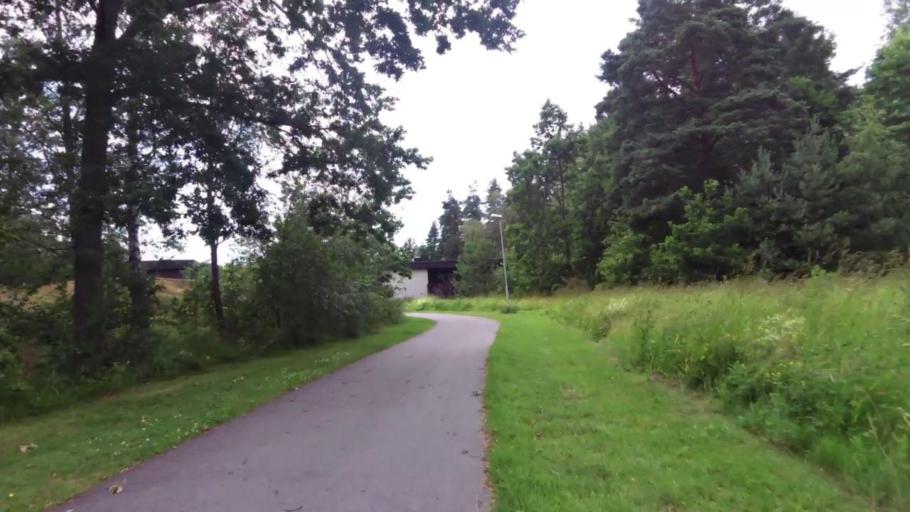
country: SE
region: OEstergoetland
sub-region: Linkopings Kommun
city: Malmslatt
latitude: 58.4150
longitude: 15.5585
